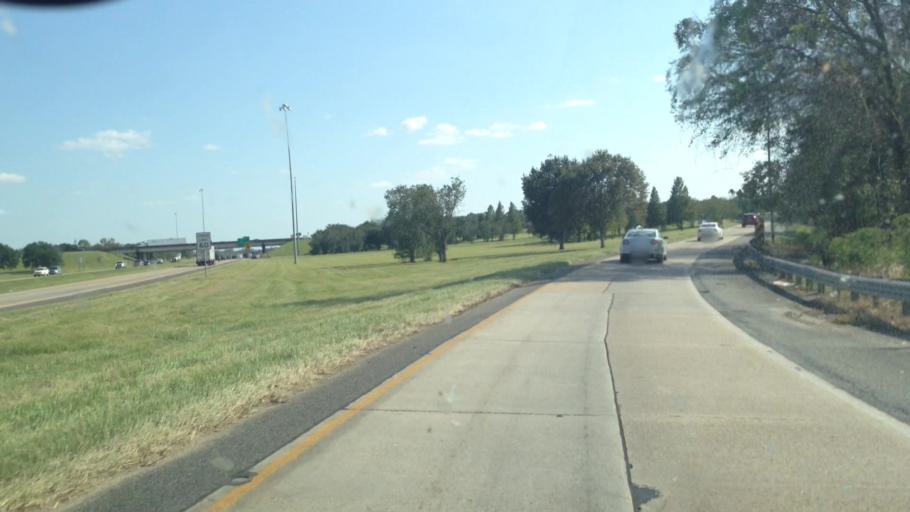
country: US
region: Louisiana
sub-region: Lafayette Parish
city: Lafayette
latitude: 30.2634
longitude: -92.0169
